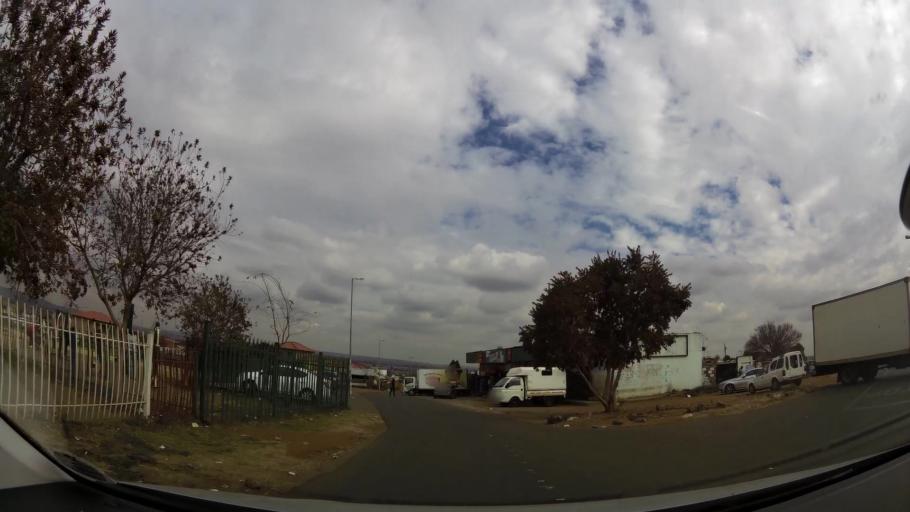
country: ZA
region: Gauteng
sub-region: City of Johannesburg Metropolitan Municipality
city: Soweto
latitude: -26.2808
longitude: 27.8579
